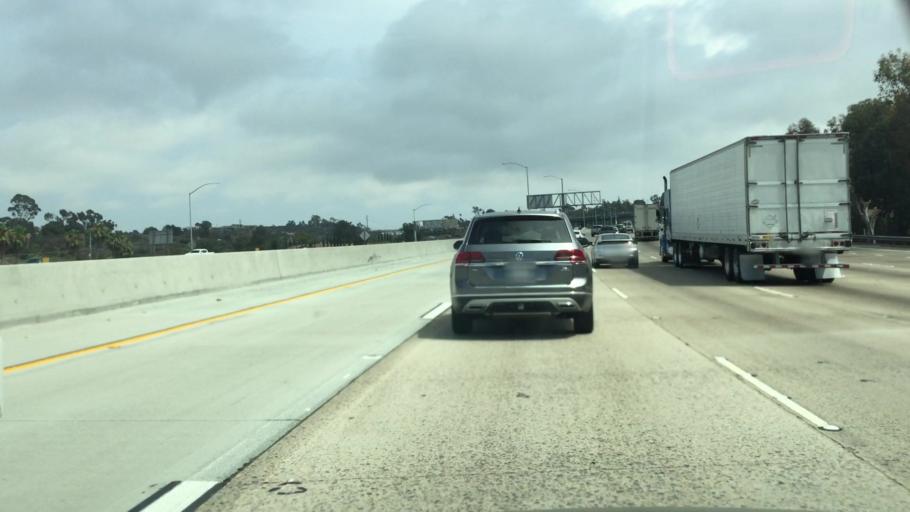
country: US
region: California
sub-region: San Diego County
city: Chula Vista
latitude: 32.6460
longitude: -117.0591
